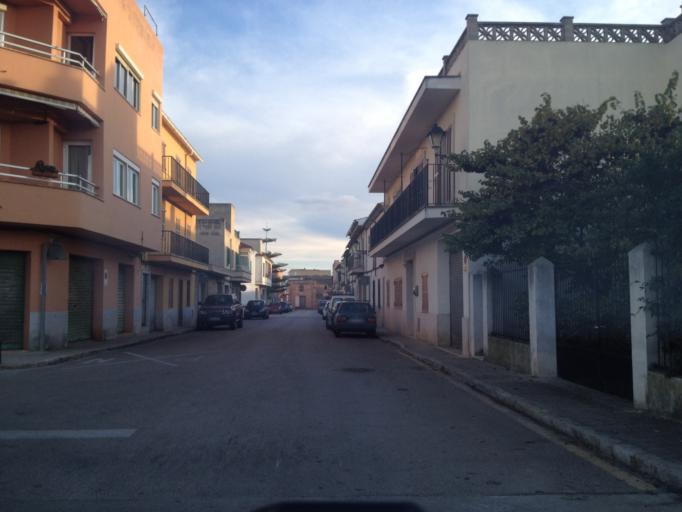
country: ES
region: Balearic Islands
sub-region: Illes Balears
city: Santa Maria del Cami
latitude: 39.6522
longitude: 2.7710
